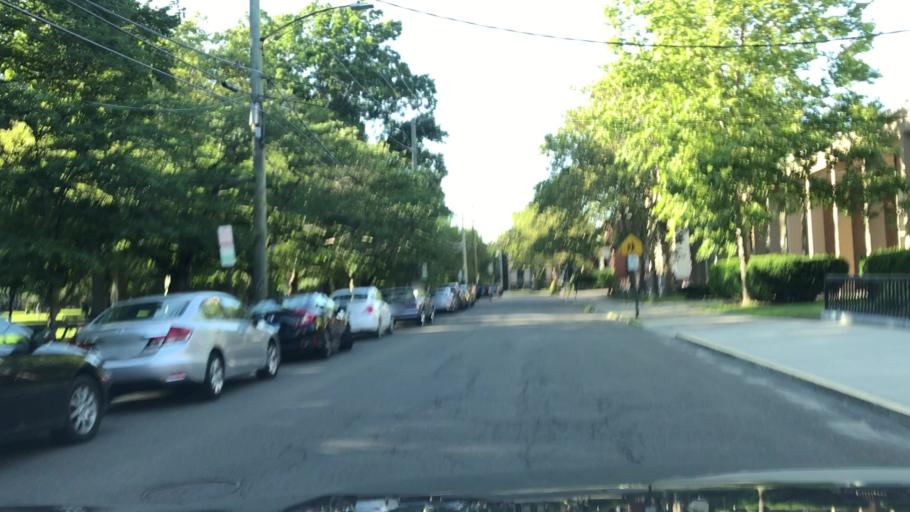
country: US
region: Connecticut
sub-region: New Haven County
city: New Haven
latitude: 41.3043
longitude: -72.9171
